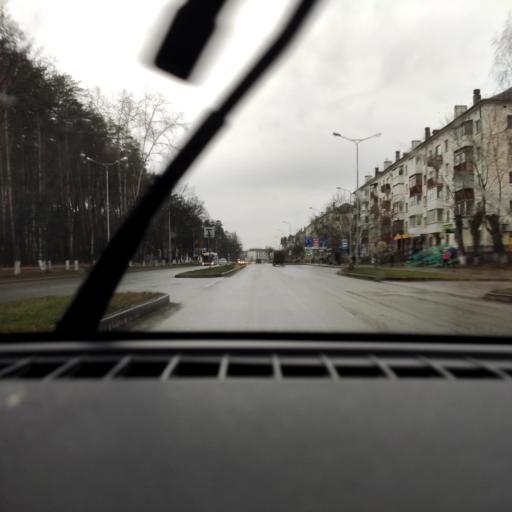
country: RU
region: Perm
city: Kultayevo
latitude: 58.0129
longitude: 55.9726
